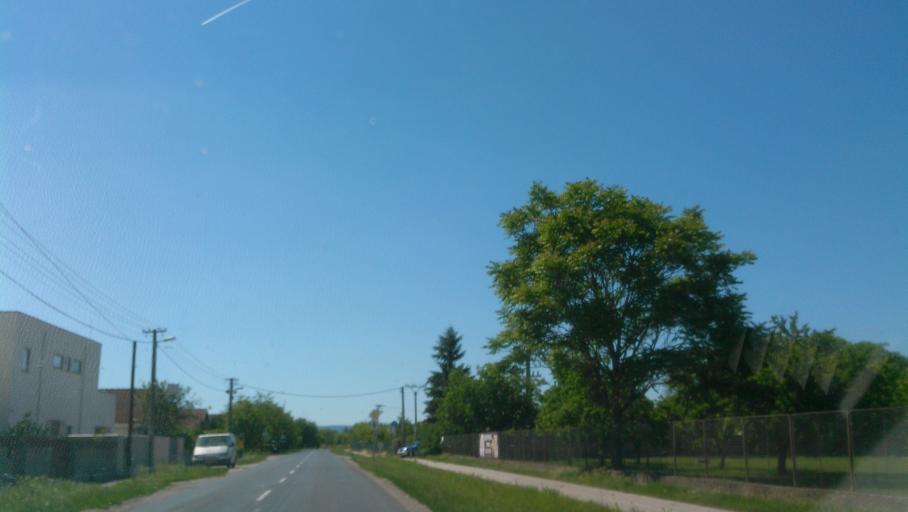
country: SK
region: Bratislavsky
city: Svaty Jur
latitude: 48.1914
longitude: 17.2877
